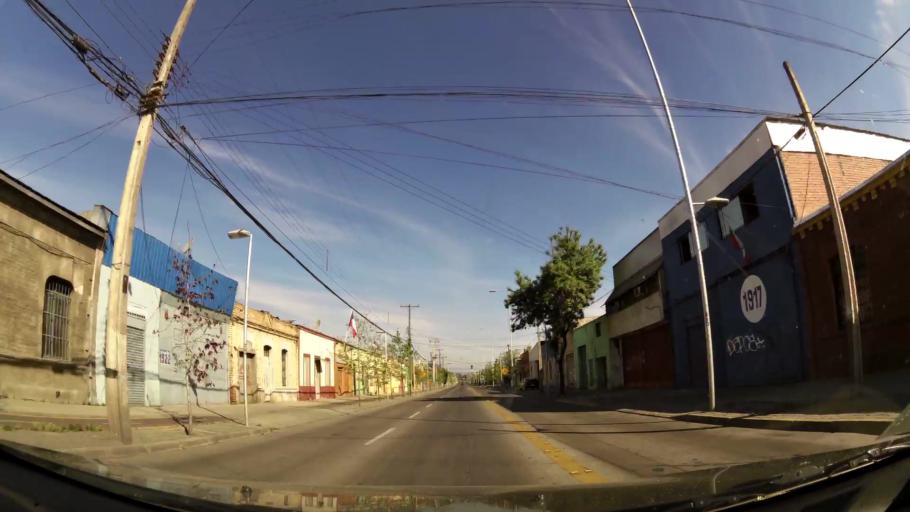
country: CL
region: Santiago Metropolitan
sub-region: Provincia de Santiago
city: Santiago
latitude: -33.4701
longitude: -70.6363
